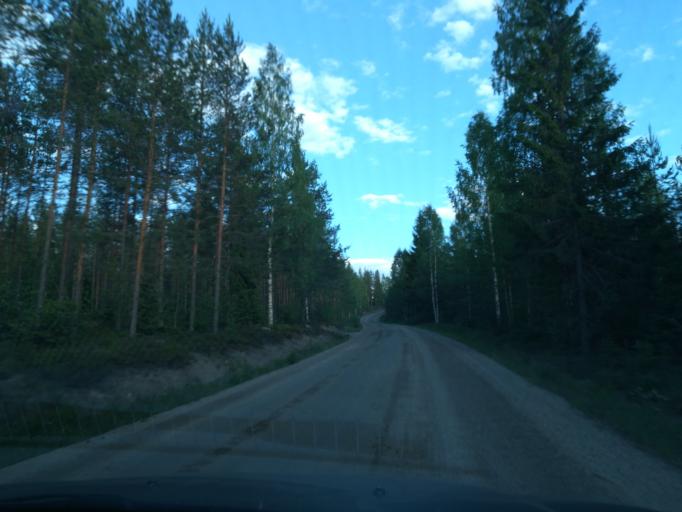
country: FI
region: Southern Savonia
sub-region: Mikkeli
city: Puumala
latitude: 61.6231
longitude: 28.1101
